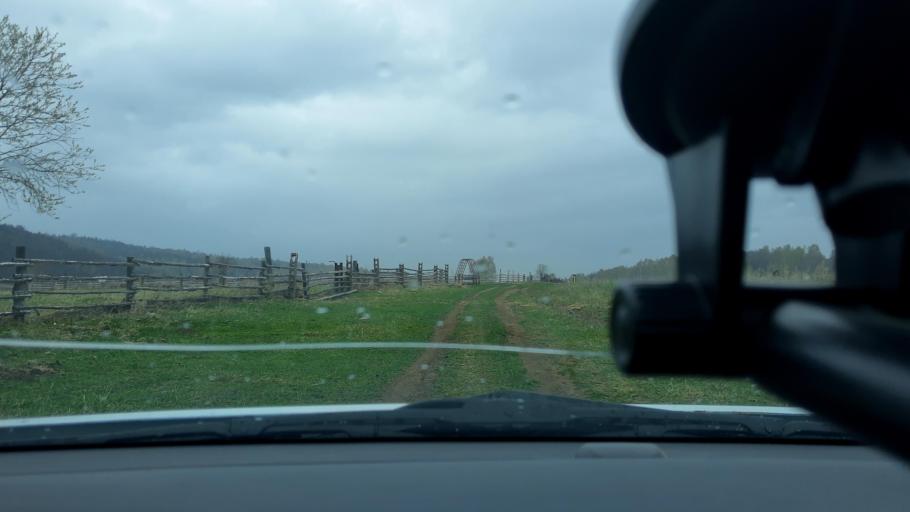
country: RU
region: Bashkortostan
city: Pavlovka
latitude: 55.4342
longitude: 56.3088
